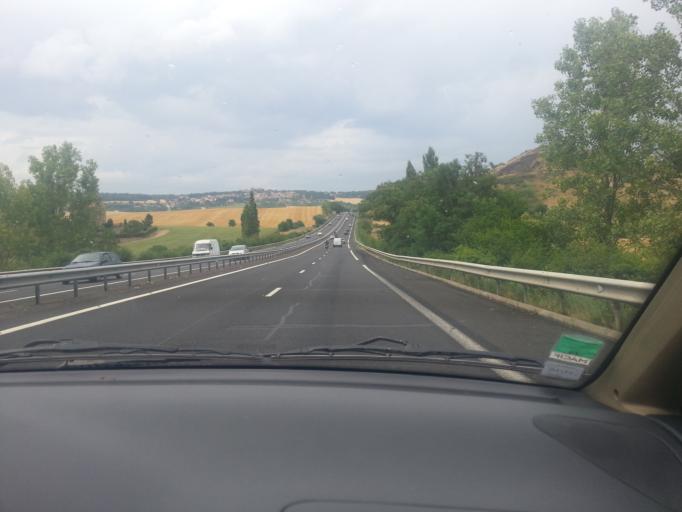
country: FR
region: Auvergne
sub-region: Departement du Puy-de-Dome
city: Le Breuil-sur-Couze
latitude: 45.4809
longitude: 3.2455
